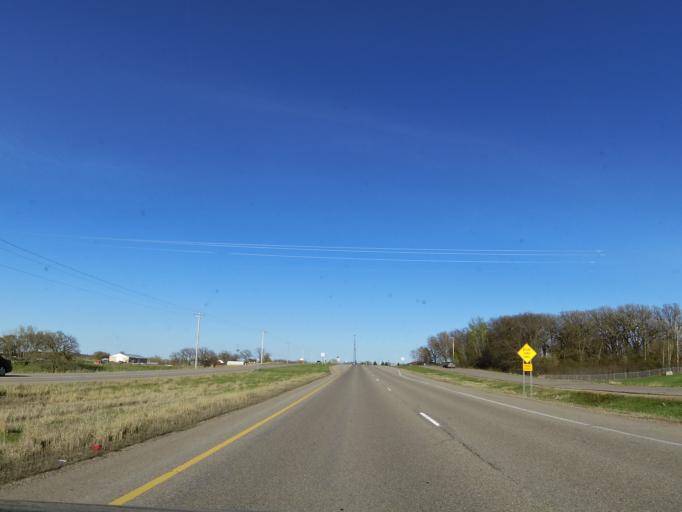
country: US
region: Minnesota
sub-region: Scott County
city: Elko New Market
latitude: 44.5733
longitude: -93.3078
